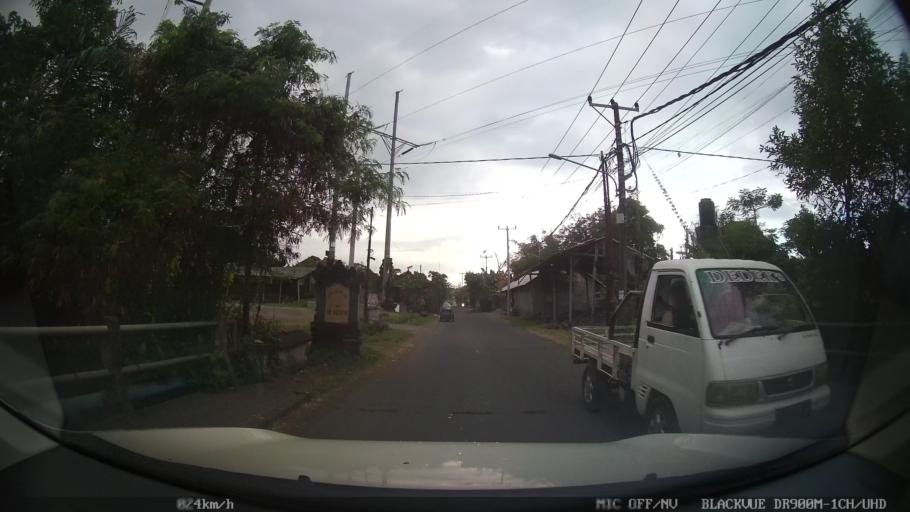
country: ID
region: Bali
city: Banjar Pasekan
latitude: -8.6286
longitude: 115.2897
